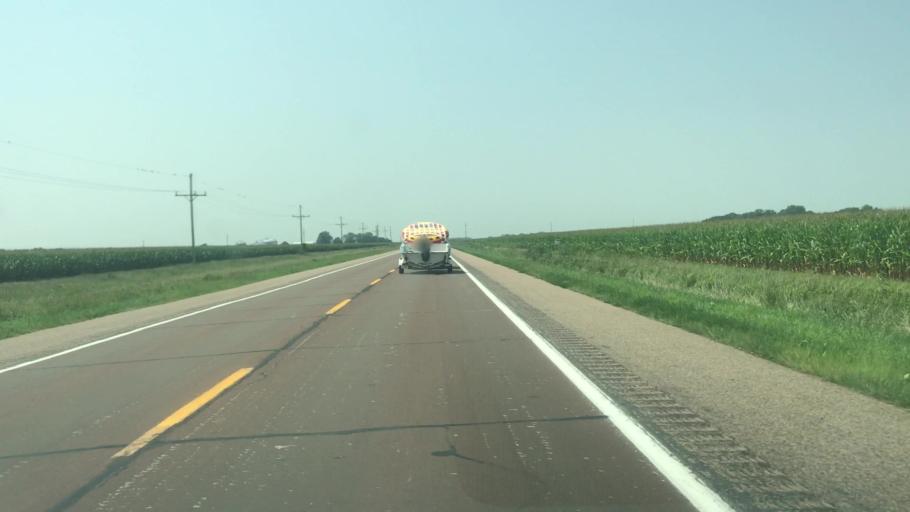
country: US
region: Nebraska
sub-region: Hall County
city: Grand Island
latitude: 40.9677
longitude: -98.4672
